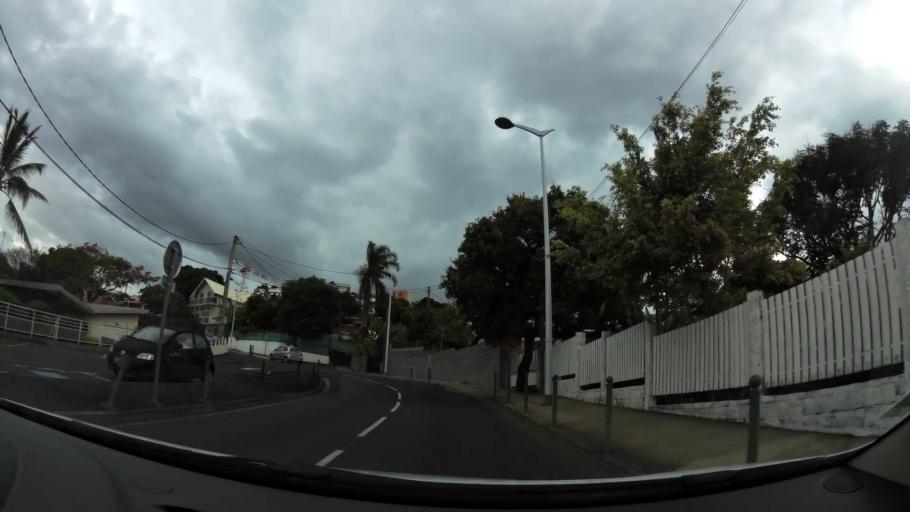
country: RE
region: Reunion
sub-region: Reunion
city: Saint-Denis
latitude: -20.8963
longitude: 55.4670
